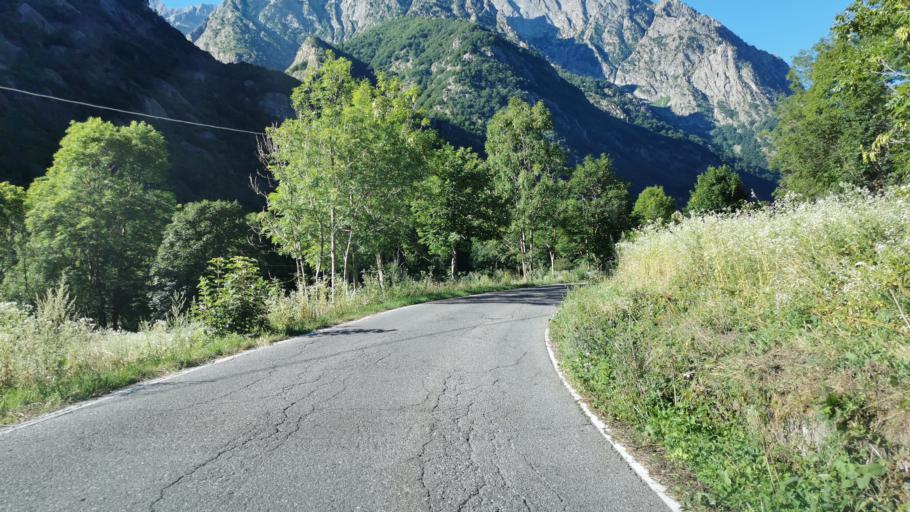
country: IT
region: Piedmont
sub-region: Provincia di Cuneo
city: Entracque
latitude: 44.2362
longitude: 7.3165
